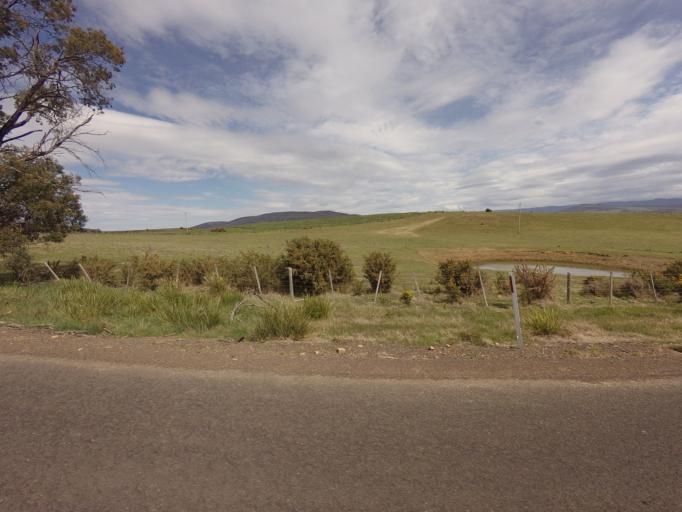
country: AU
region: Tasmania
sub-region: Northern Midlands
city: Evandale
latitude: -41.8932
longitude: 147.4040
